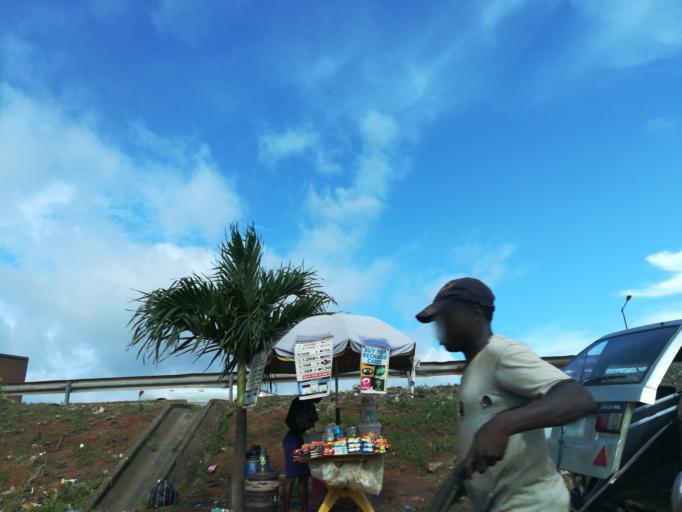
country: NG
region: Lagos
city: Agege
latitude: 6.6071
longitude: 3.3099
